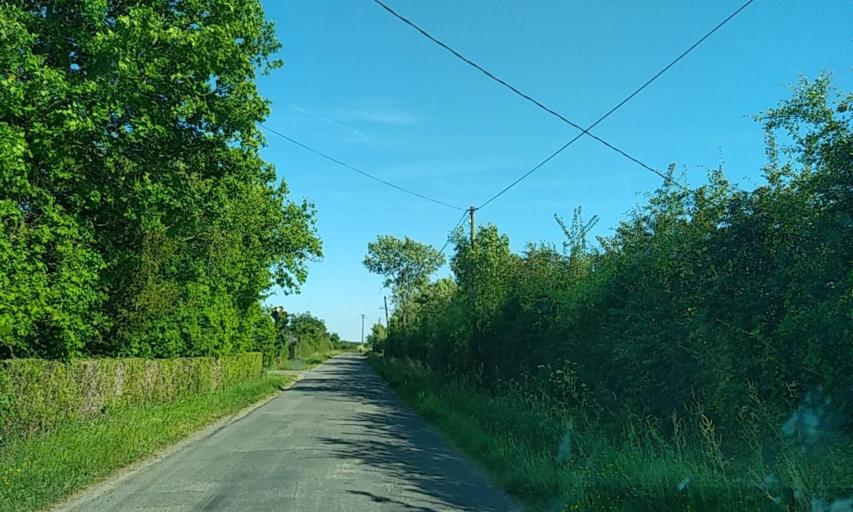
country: FR
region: Poitou-Charentes
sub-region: Departement des Deux-Sevres
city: Boisme
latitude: 46.7993
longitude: -0.4384
